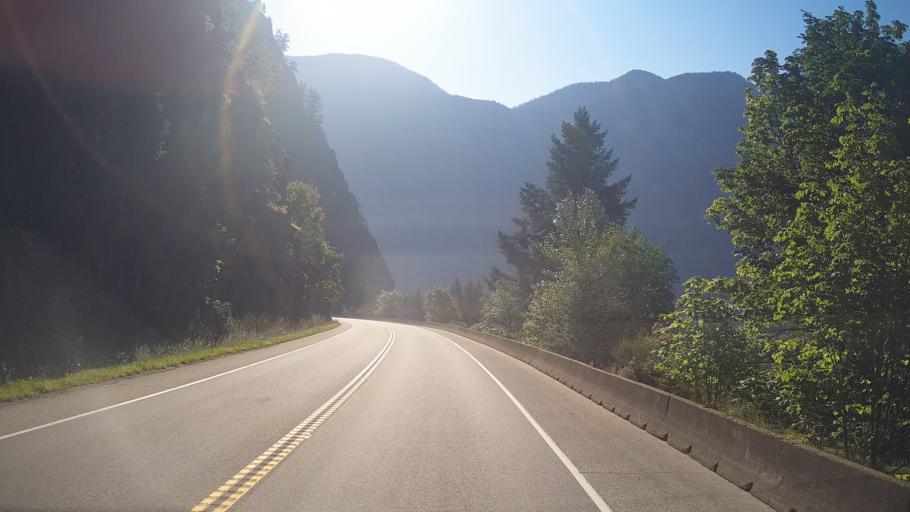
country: CA
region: British Columbia
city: Hope
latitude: 49.5633
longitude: -121.4202
